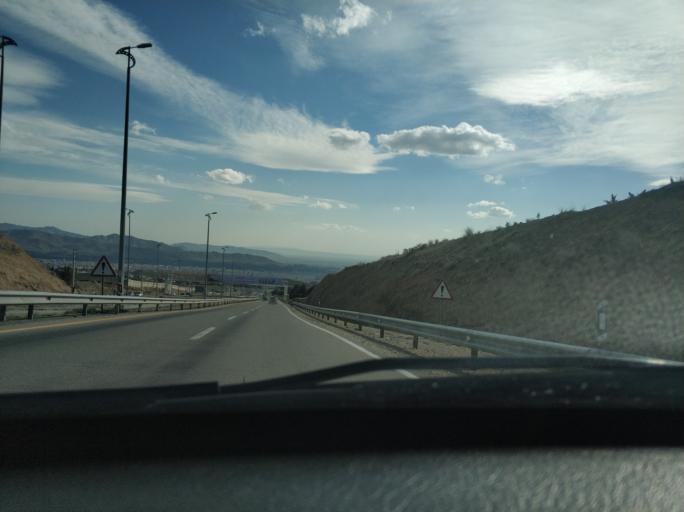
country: IR
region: Tehran
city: Tajrish
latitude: 35.7866
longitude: 51.5660
